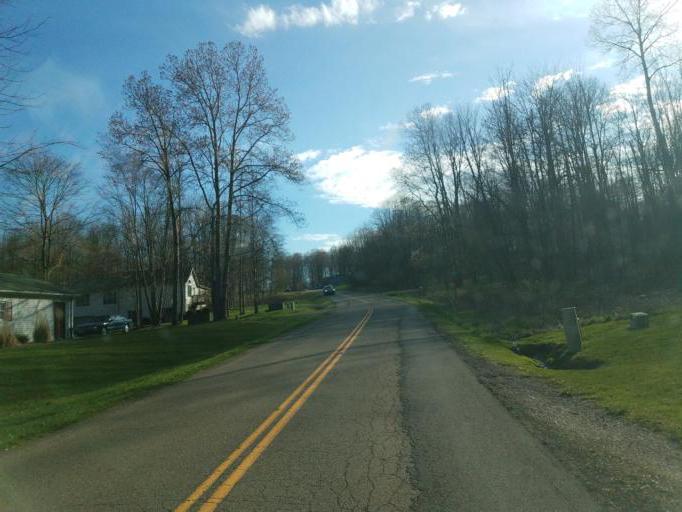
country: US
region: Ohio
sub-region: Knox County
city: Gambier
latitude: 40.4536
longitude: -82.3535
